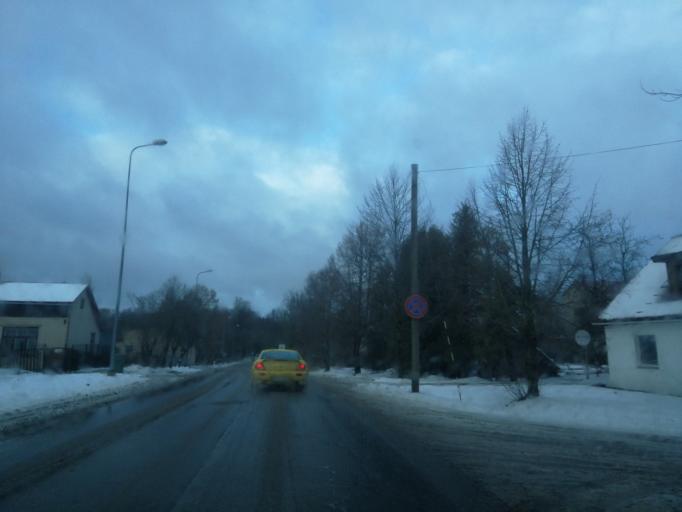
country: LV
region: Cesu Rajons
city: Cesis
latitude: 57.3030
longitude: 25.2688
